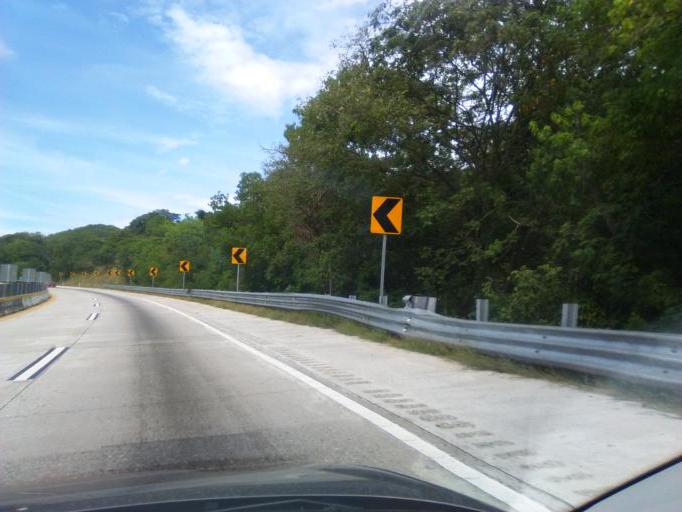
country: MX
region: Guerrero
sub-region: Chilpancingo de los Bravo
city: Julian Blanco (Dos Caminos)
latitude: 17.1993
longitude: -99.5325
